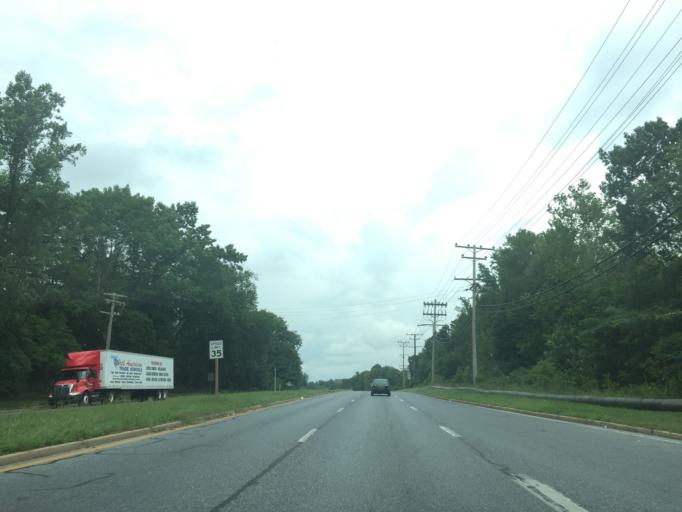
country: US
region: Maryland
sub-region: Baltimore County
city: Woodlawn
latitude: 39.3046
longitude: -76.7131
